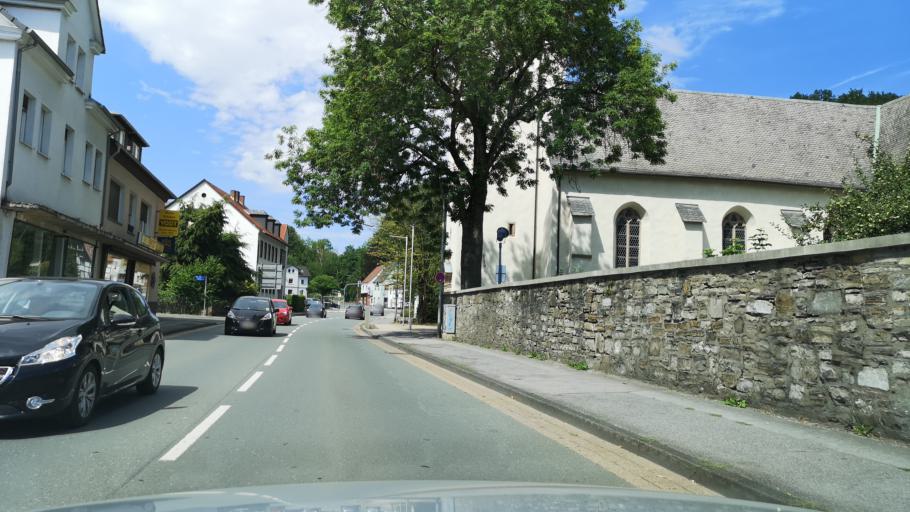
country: DE
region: North Rhine-Westphalia
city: Hemer
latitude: 51.3952
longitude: 7.7602
